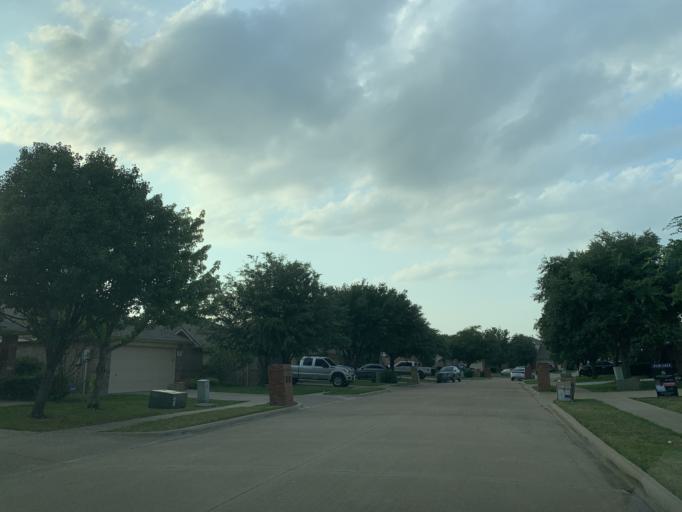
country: US
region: Texas
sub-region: Tarrant County
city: Keller
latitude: 32.9402
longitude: -97.2616
